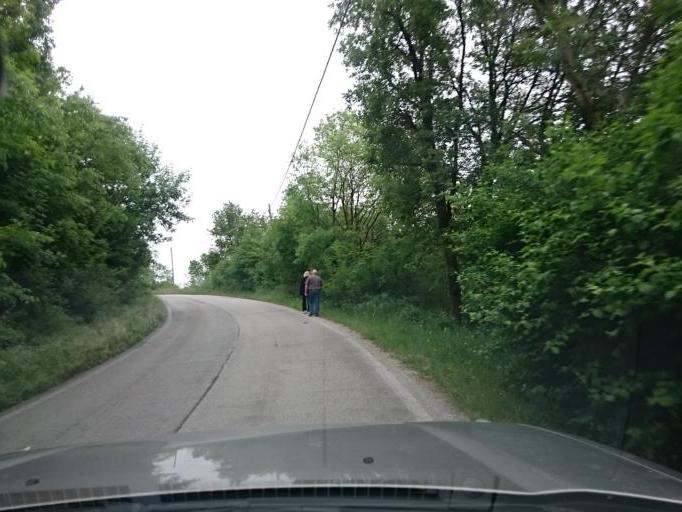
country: IT
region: Veneto
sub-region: Provincia di Padova
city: Montegrotto Terme
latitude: 45.3157
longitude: 11.7696
